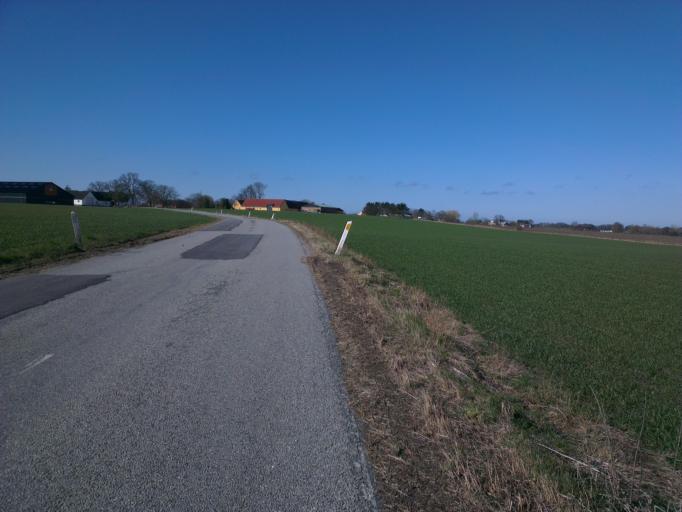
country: DK
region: Capital Region
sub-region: Frederikssund Kommune
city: Frederikssund
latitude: 55.8798
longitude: 12.1021
